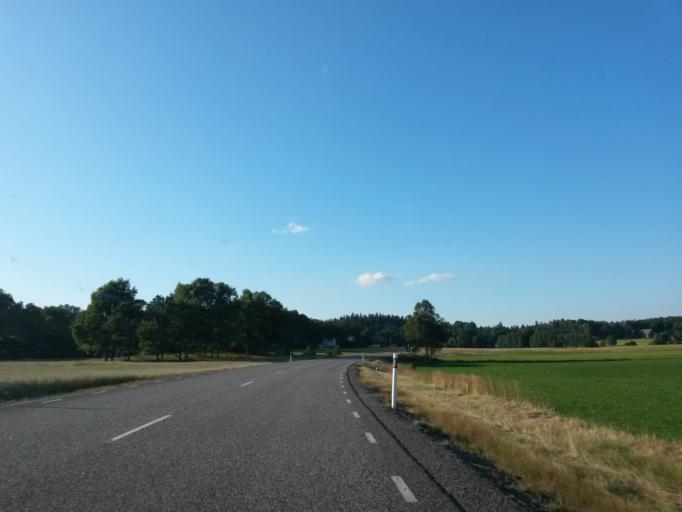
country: SE
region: Vaestra Goetaland
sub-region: Vargarda Kommun
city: Jonstorp
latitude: 58.0292
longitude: 12.6327
